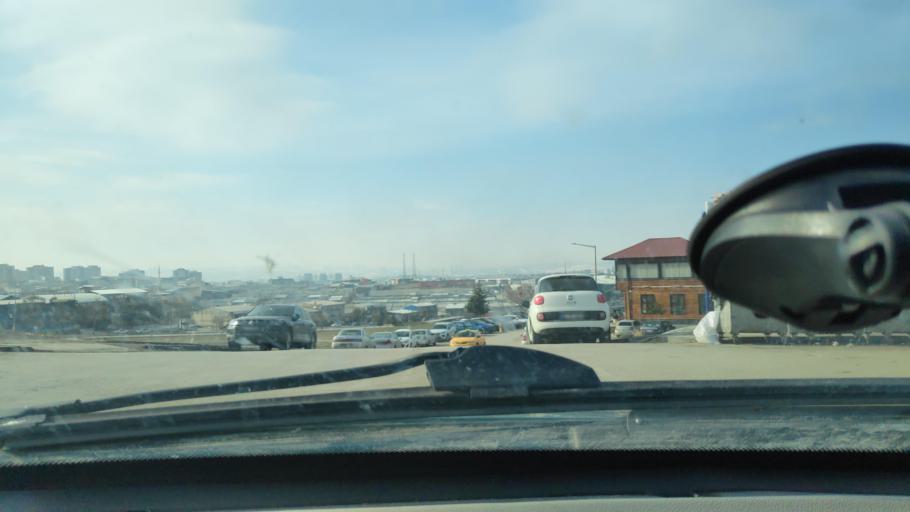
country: TR
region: Ankara
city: Batikent
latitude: 39.9947
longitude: 32.7504
